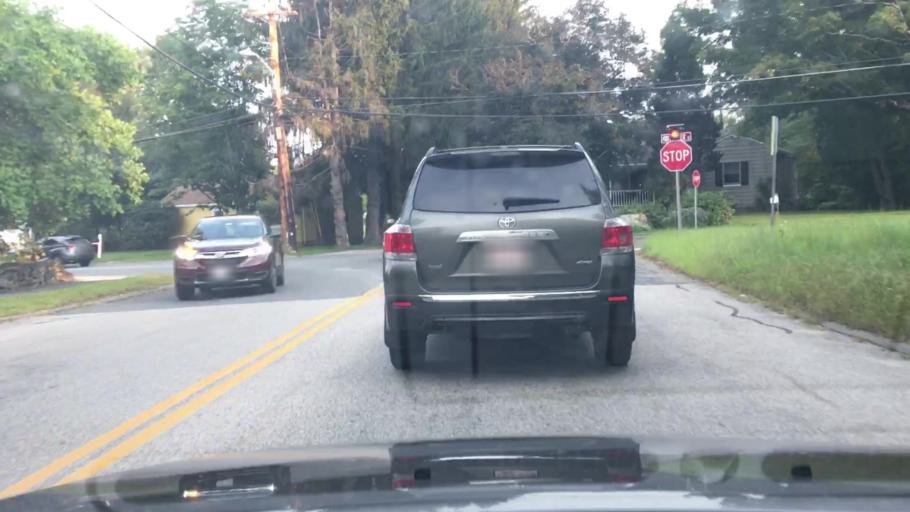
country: US
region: Massachusetts
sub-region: Worcester County
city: Westborough
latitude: 42.2695
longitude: -71.6405
